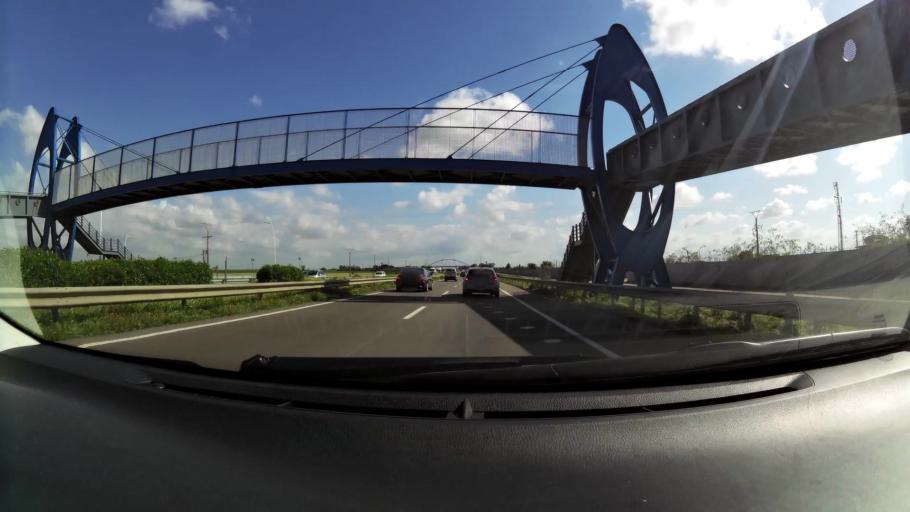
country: MA
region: Chaouia-Ouardigha
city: Nouaseur
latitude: 33.3750
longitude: -7.6215
